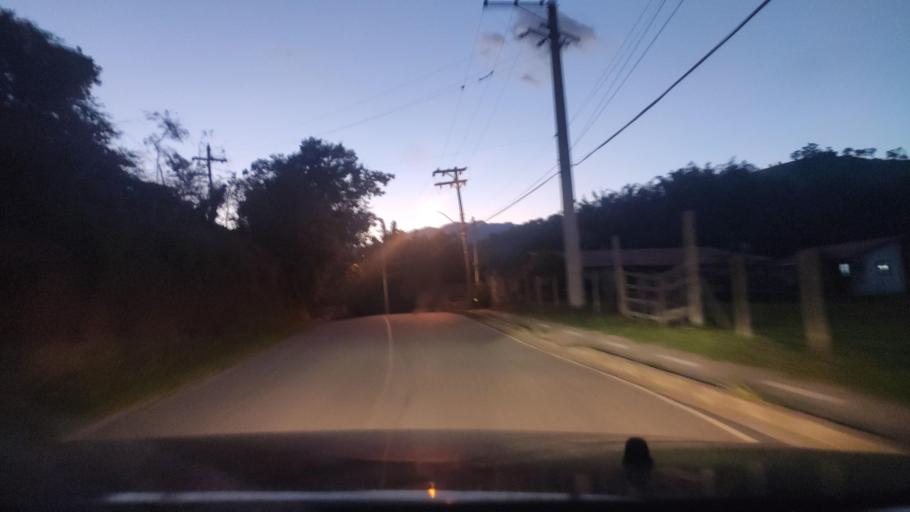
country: BR
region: Minas Gerais
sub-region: Paraisopolis
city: Paraisopolis
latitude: -22.6969
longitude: -45.7479
